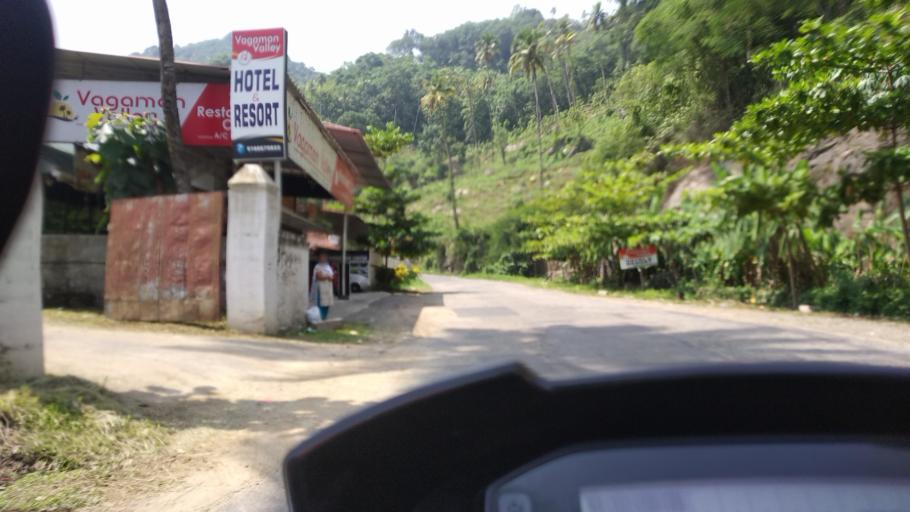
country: IN
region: Kerala
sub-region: Kottayam
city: Erattupetta
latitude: 9.6876
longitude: 76.8274
